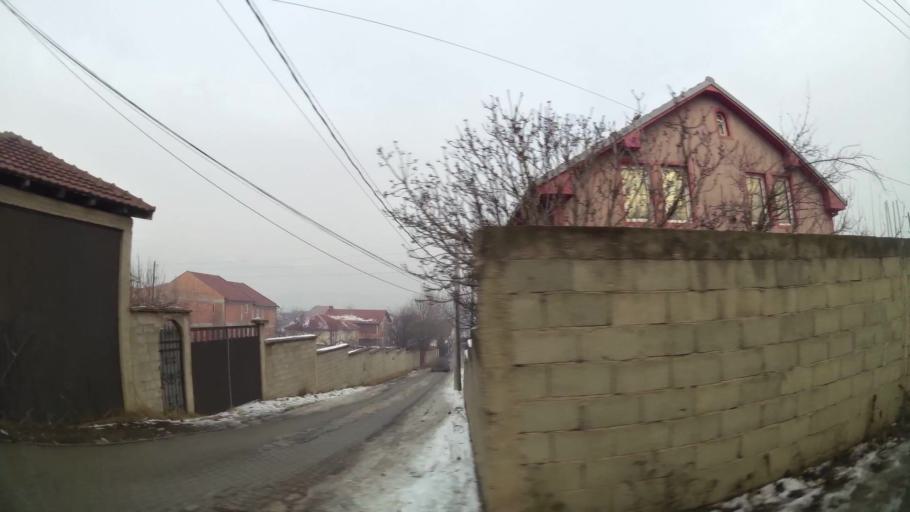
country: MK
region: Suto Orizari
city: Suto Orizare
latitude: 42.0337
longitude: 21.4159
